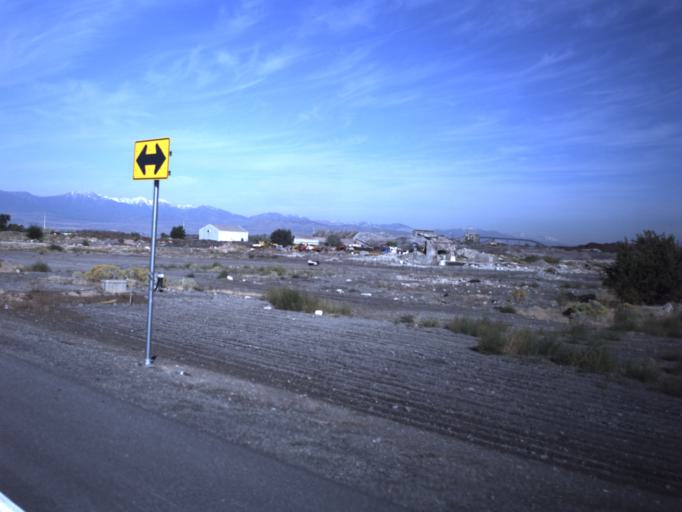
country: US
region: Utah
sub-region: Utah County
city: Lindon
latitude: 40.3118
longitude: -111.7420
